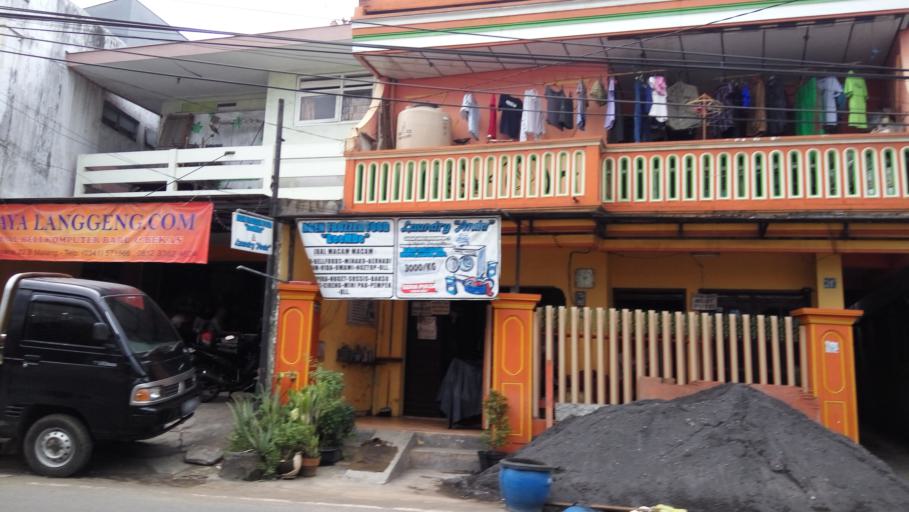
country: ID
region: East Java
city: Malang
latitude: -7.9493
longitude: 112.6089
